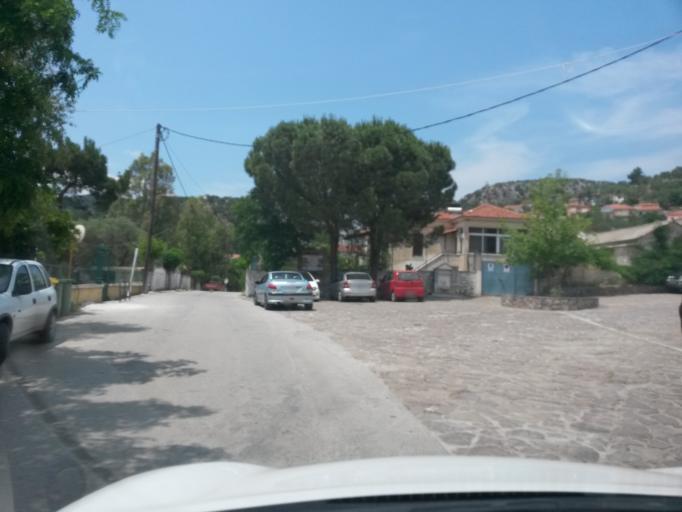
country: GR
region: North Aegean
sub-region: Nomos Lesvou
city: Pamfylla
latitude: 39.1810
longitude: 26.4190
